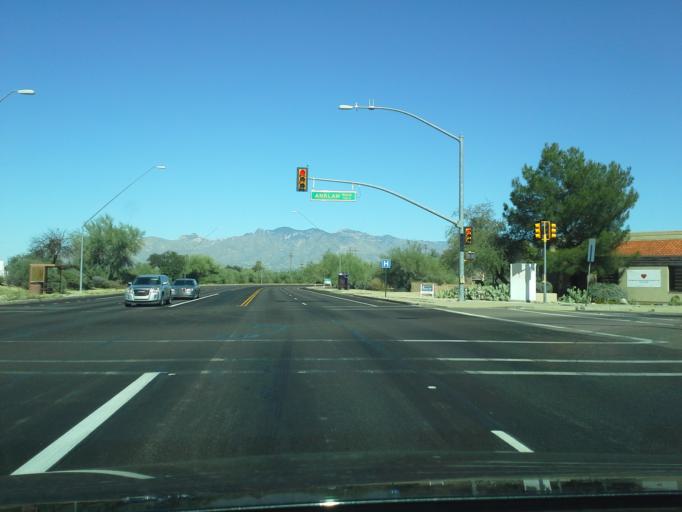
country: US
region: Arizona
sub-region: Pima County
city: South Tucson
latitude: 32.2262
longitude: -111.0057
